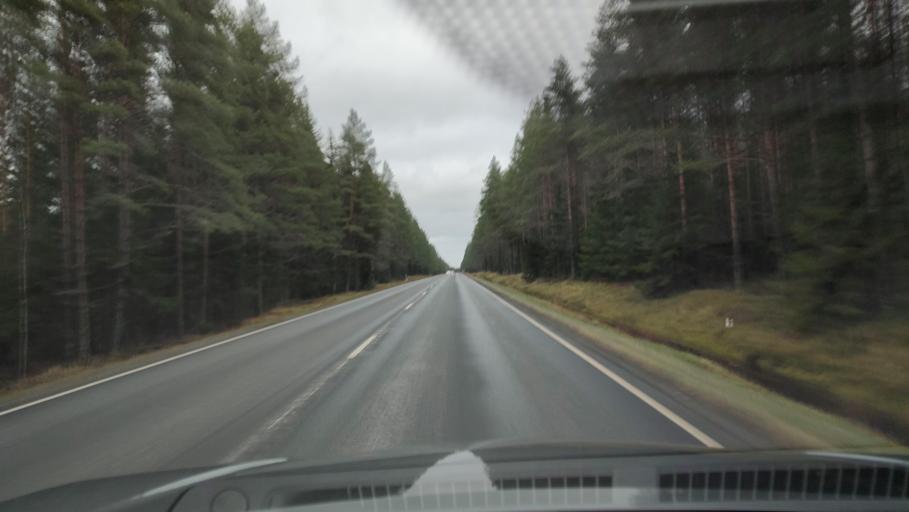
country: FI
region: Southern Ostrobothnia
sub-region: Seinaejoki
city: Kurikka
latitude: 62.5310
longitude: 22.3282
